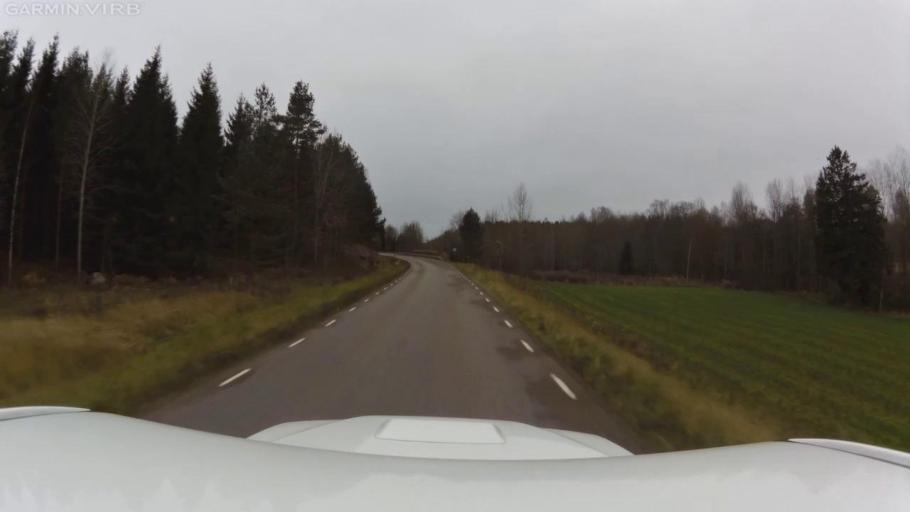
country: SE
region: OEstergoetland
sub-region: Linkopings Kommun
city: Vikingstad
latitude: 58.2254
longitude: 15.3958
